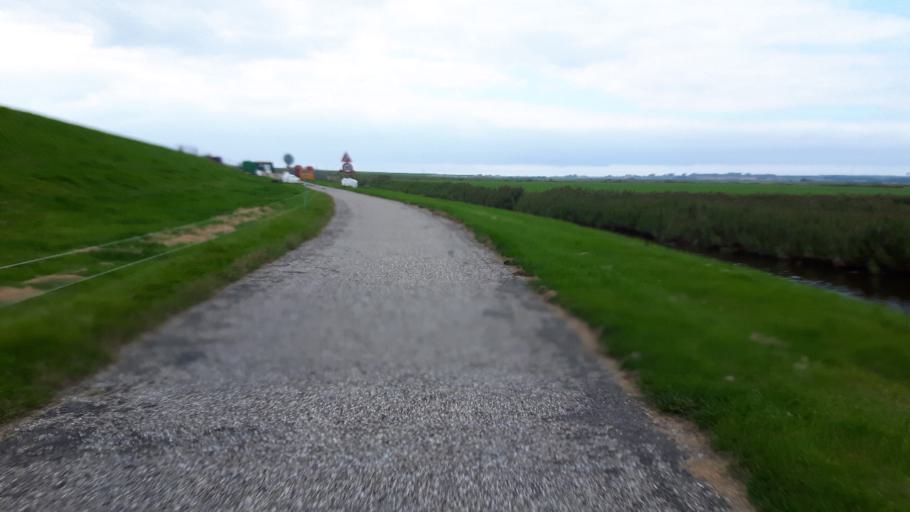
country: NL
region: Friesland
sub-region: Gemeente Ameland
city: Nes
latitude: 53.4395
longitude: 5.8118
